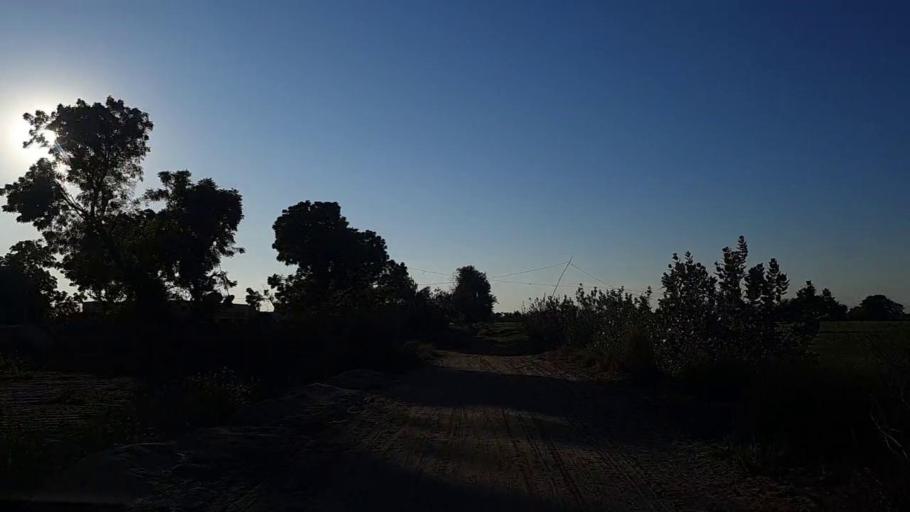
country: PK
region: Sindh
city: Sanghar
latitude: 26.1481
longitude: 68.9173
